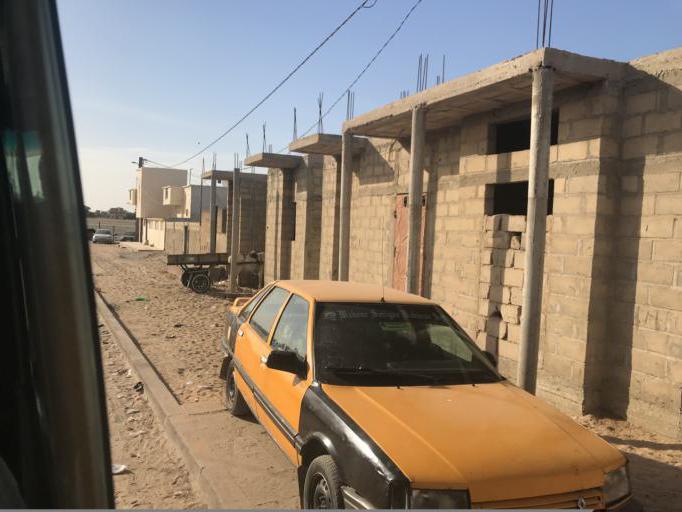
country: SN
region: Saint-Louis
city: Saint-Louis
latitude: 15.9935
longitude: -16.4917
